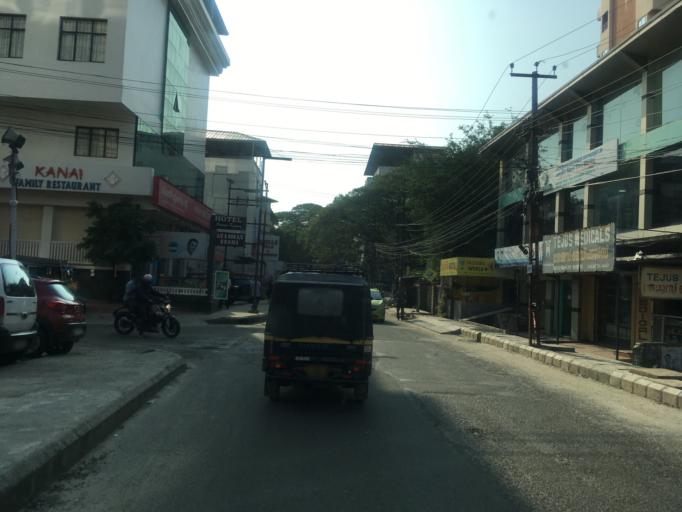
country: IN
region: Kerala
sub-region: Ernakulam
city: Cochin
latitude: 9.9719
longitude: 76.2835
